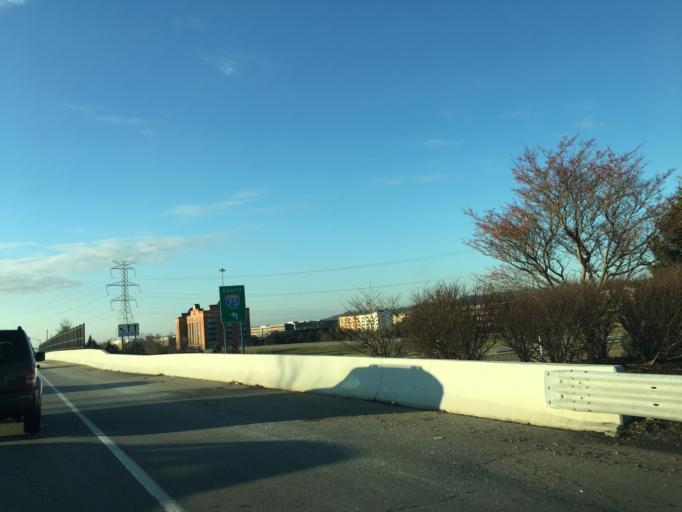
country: US
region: Ohio
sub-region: Butler County
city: Beckett Ridge
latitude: 39.3219
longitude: -84.4229
